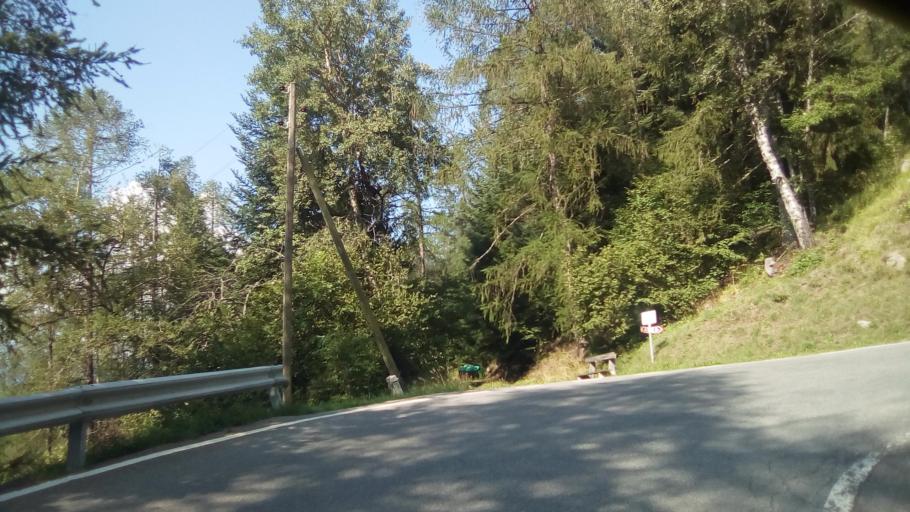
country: CH
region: Valais
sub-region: Martigny District
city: Martigny-Combe
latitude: 46.0659
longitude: 7.0778
